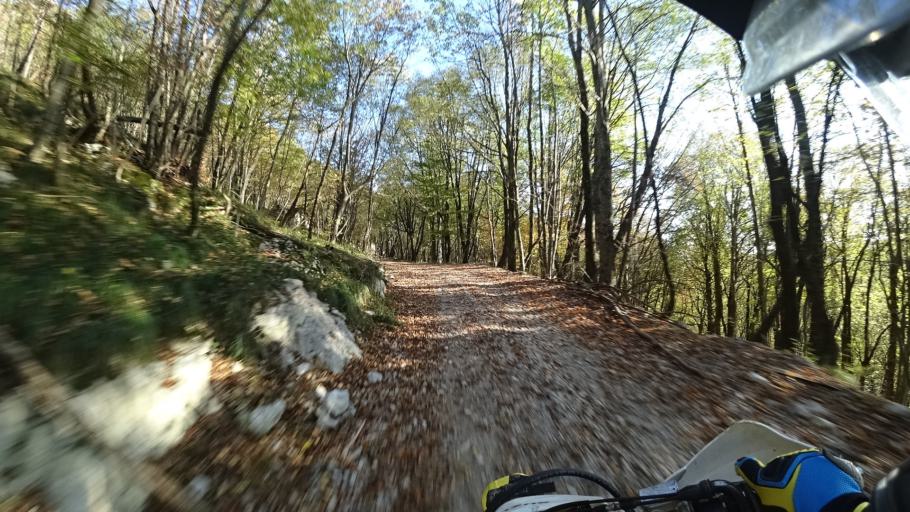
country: HR
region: Primorsko-Goranska
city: Klana
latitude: 45.4877
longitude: 14.4126
